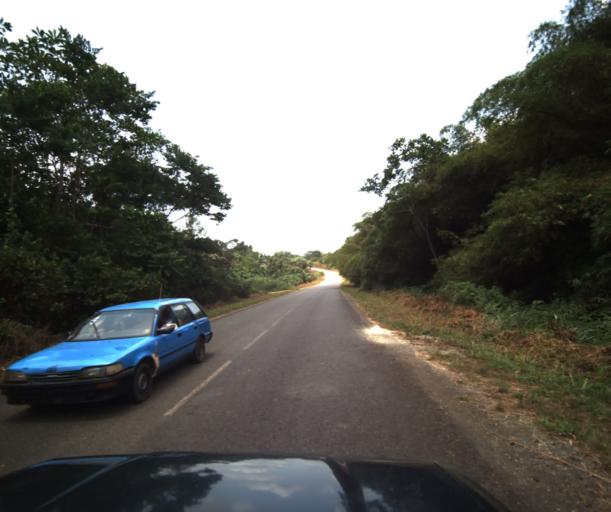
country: CM
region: Centre
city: Eseka
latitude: 3.7046
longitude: 10.7897
